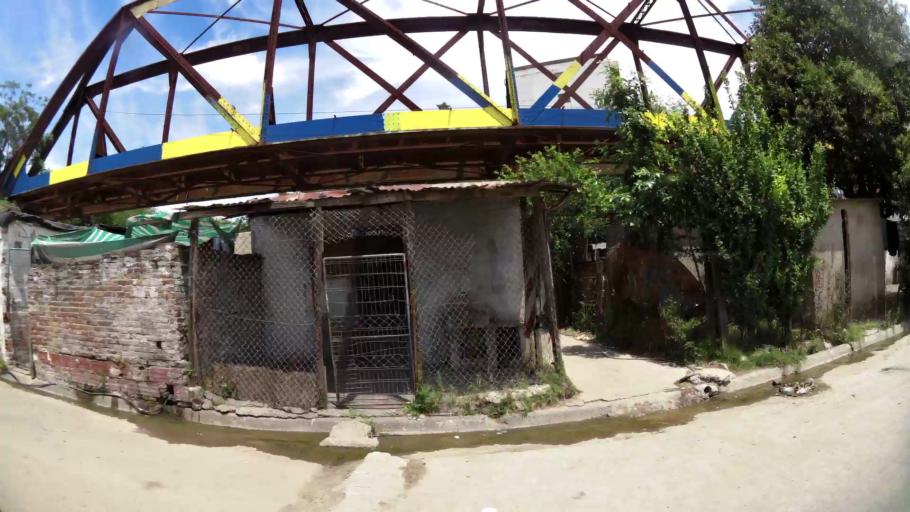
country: AR
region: Santa Fe
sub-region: Departamento de Rosario
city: Rosario
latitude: -32.9814
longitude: -60.6261
